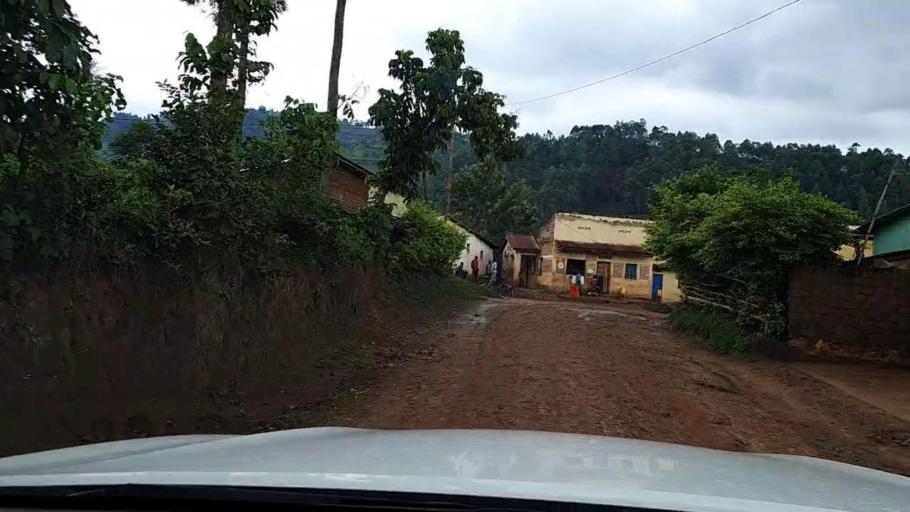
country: RW
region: Western Province
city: Cyangugu
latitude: -2.5653
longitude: 29.0341
